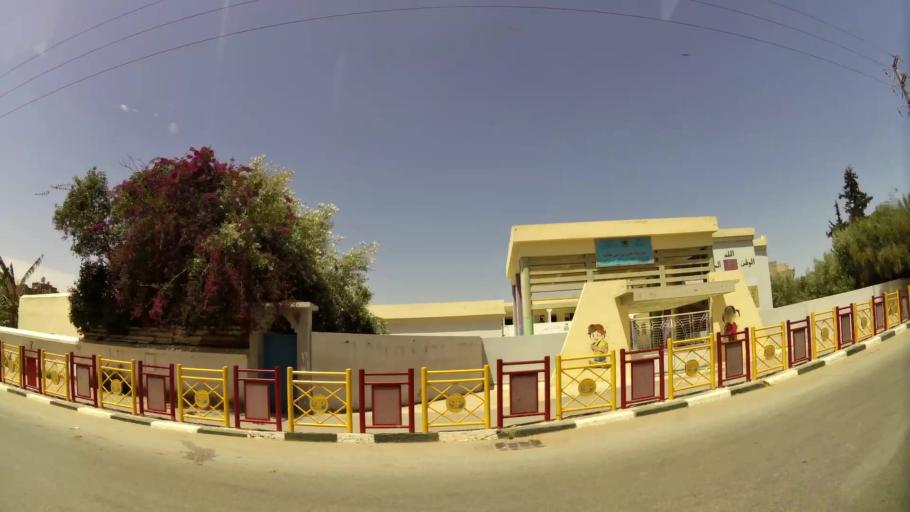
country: MA
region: Rabat-Sale-Zemmour-Zaer
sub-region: Khemisset
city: Khemisset
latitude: 33.8301
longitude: -6.0777
